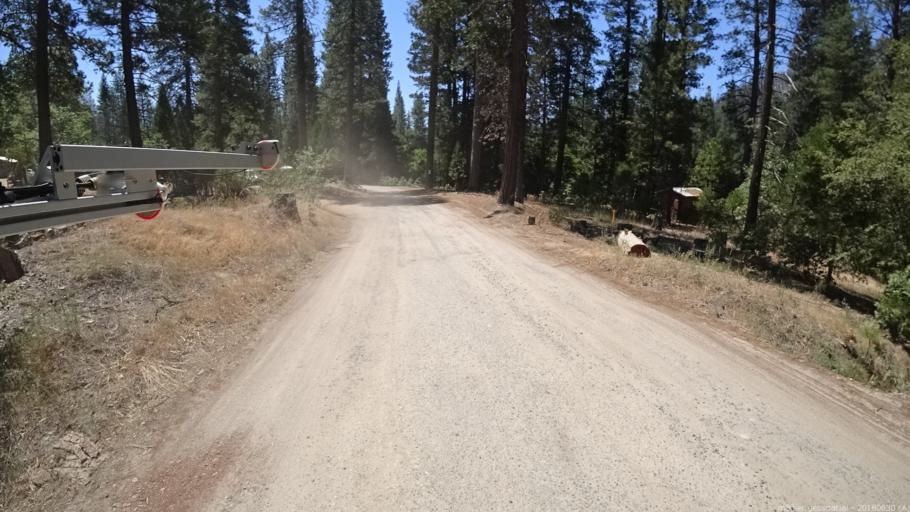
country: US
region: California
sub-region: Fresno County
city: Auberry
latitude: 37.3536
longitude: -119.3407
